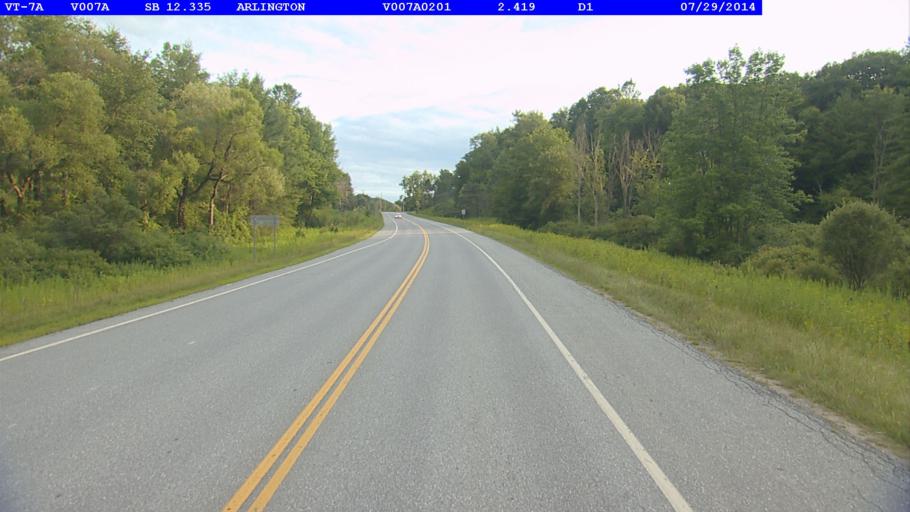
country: US
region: Vermont
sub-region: Bennington County
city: Arlington
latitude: 43.0548
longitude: -73.1633
